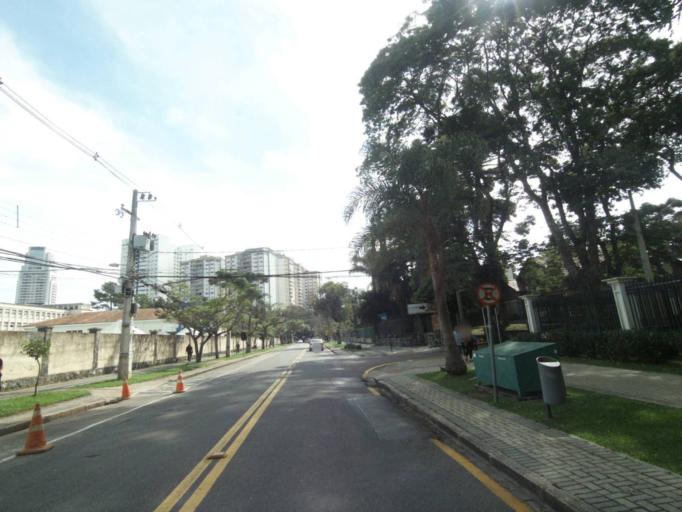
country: BR
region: Parana
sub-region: Curitiba
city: Curitiba
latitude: -25.4232
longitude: -49.2650
